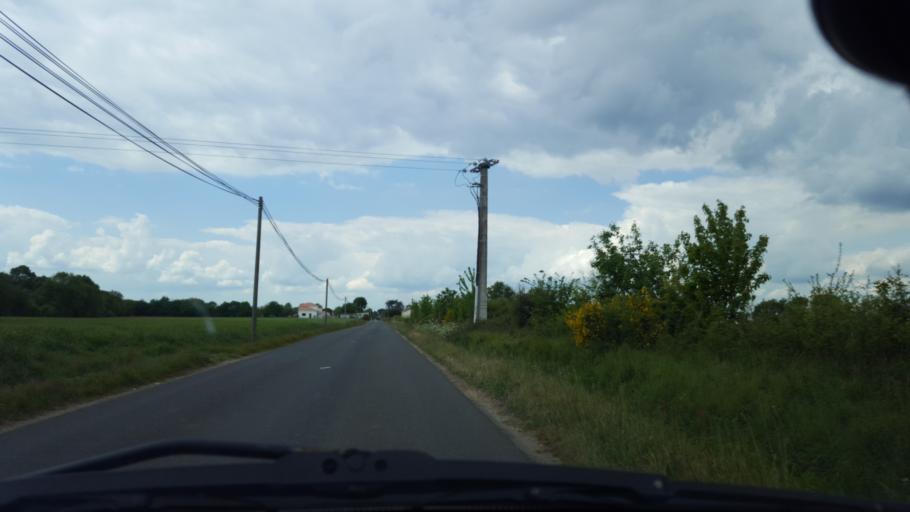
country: FR
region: Pays de la Loire
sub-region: Departement de la Loire-Atlantique
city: Saint-Philbert-de-Grand-Lieu
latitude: 47.0445
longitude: -1.6164
